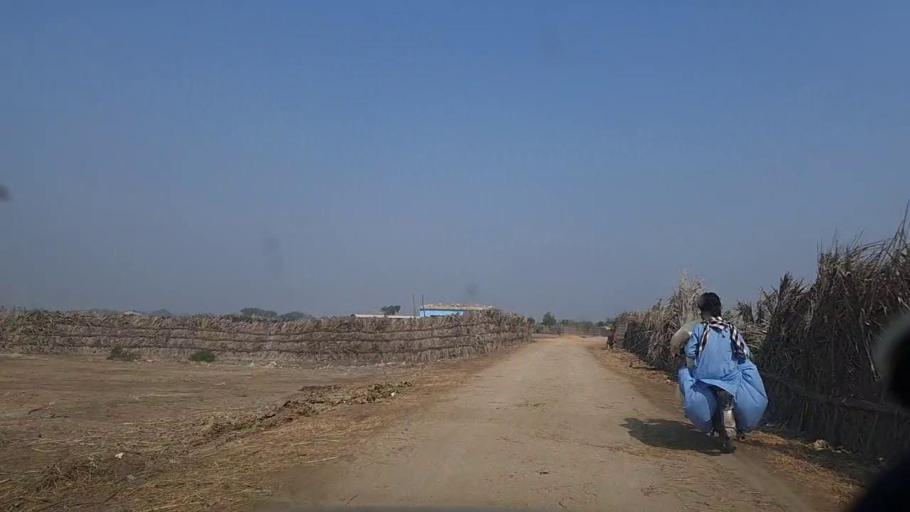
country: PK
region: Sindh
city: Thatta
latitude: 24.6501
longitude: 67.9054
